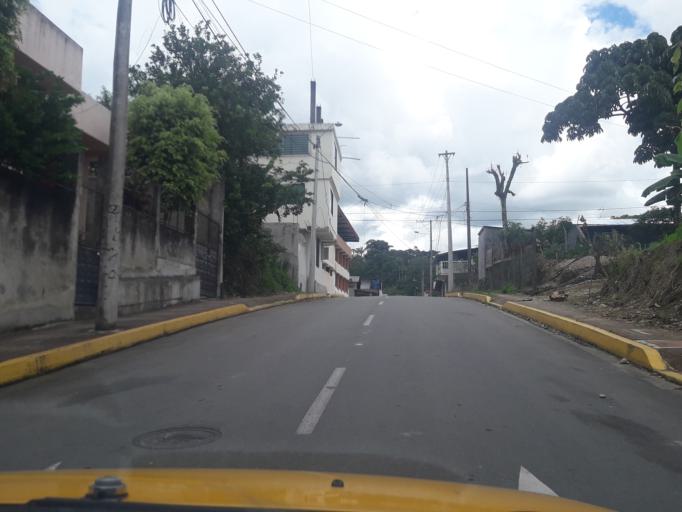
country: EC
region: Napo
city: Tena
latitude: -1.0050
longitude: -77.8153
